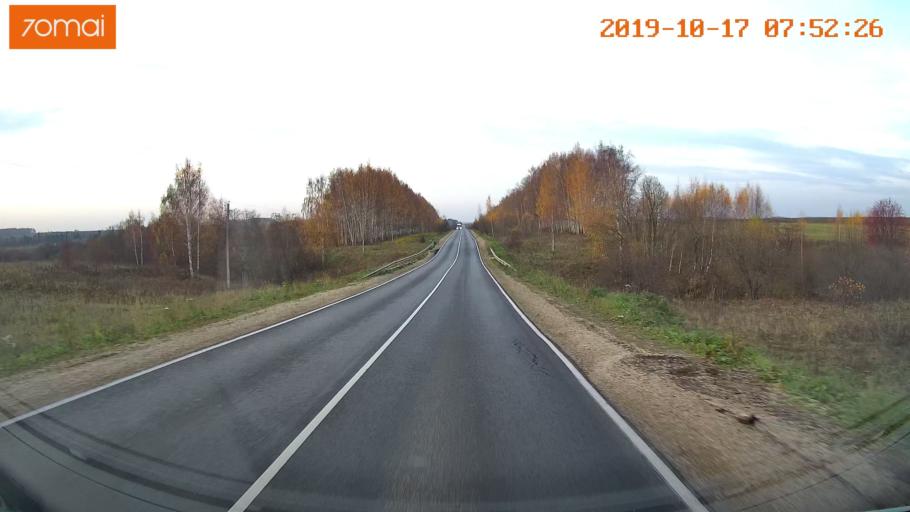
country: RU
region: Vladimir
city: Yur'yev-Pol'skiy
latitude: 56.4726
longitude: 39.6406
